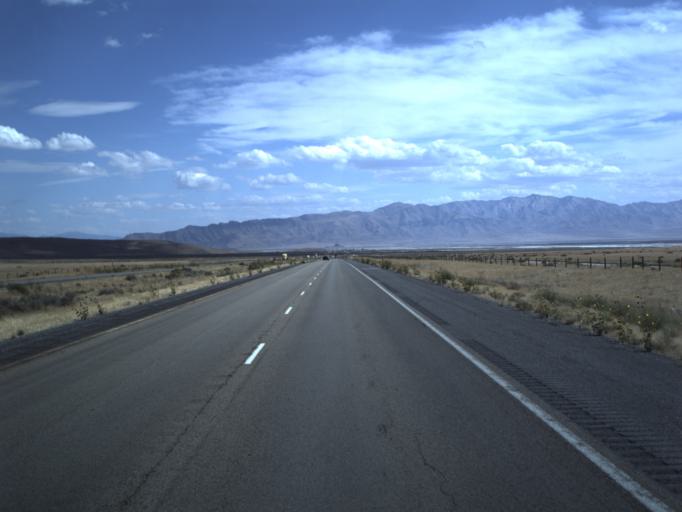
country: US
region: Utah
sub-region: Tooele County
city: Grantsville
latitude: 40.7967
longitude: -112.8436
